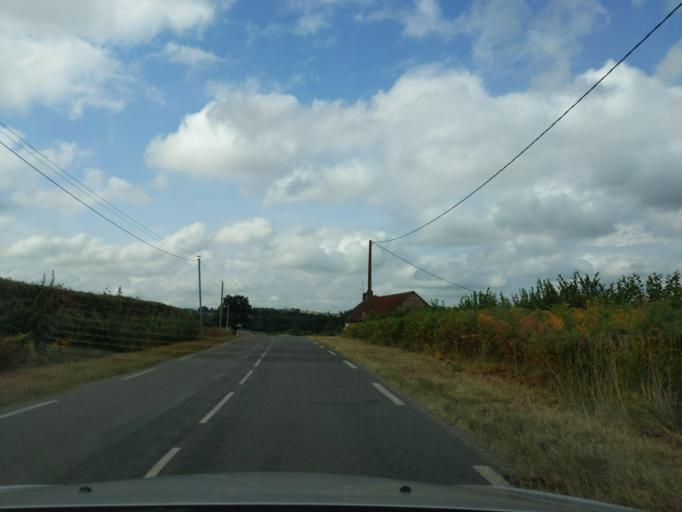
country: FR
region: Bourgogne
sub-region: Departement de la Nievre
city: Luzy
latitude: 46.7339
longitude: 3.9217
